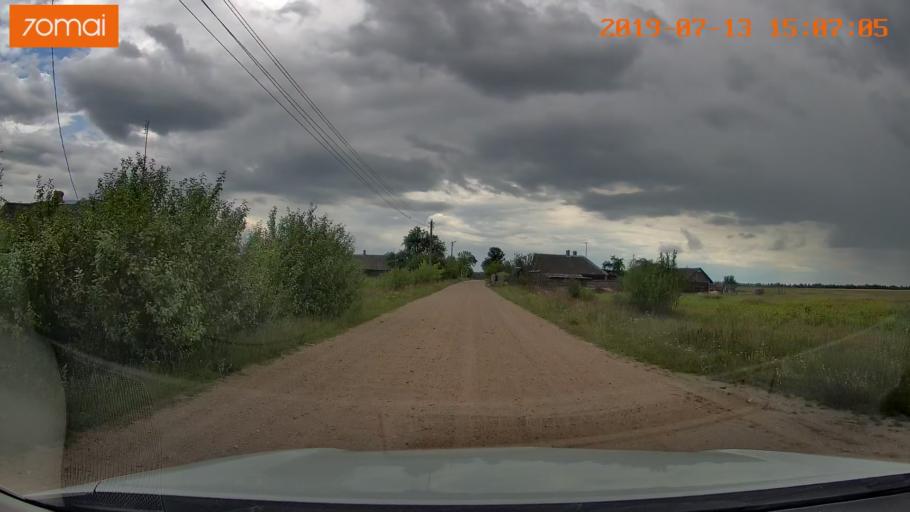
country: BY
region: Mogilev
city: Hlusha
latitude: 53.1934
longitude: 28.7566
